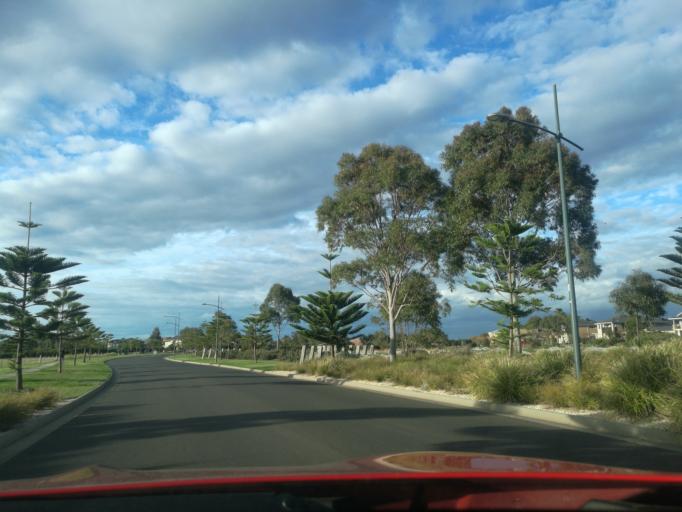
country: AU
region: Victoria
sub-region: Wyndham
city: Point Cook
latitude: -37.9168
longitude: 144.7757
